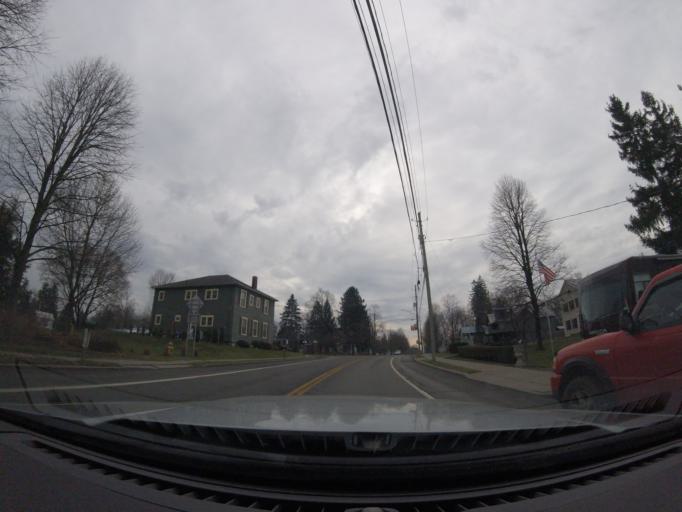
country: US
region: New York
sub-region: Schuyler County
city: Watkins Glen
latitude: 42.4178
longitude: -76.8495
